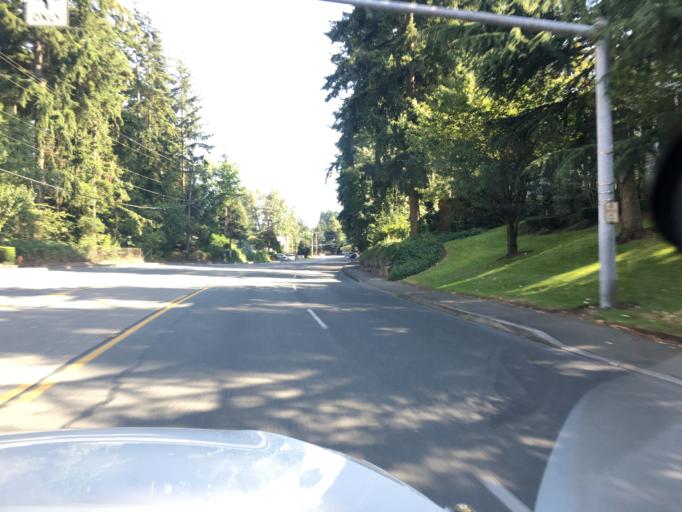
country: US
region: Washington
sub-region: Snohomish County
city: Esperance
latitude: 47.7876
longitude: -122.3539
